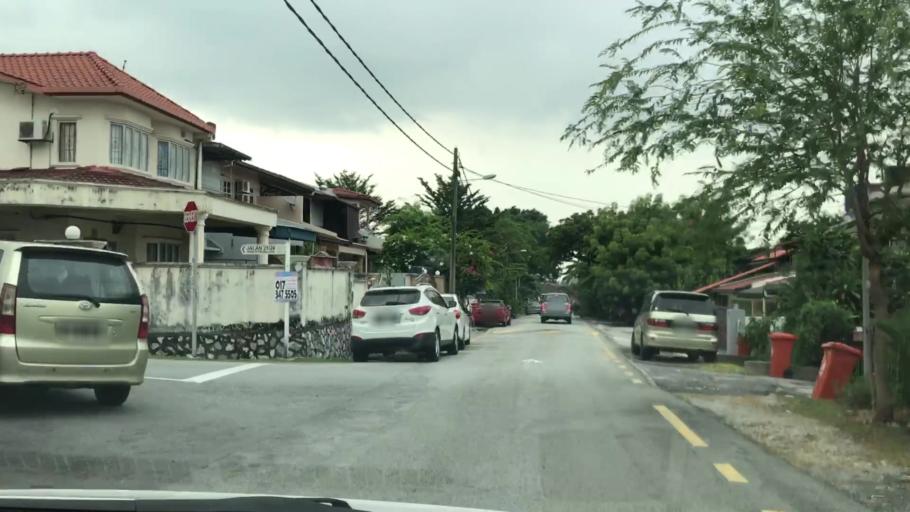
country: MY
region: Selangor
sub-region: Petaling
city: Petaling Jaya
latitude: 3.1093
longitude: 101.6201
